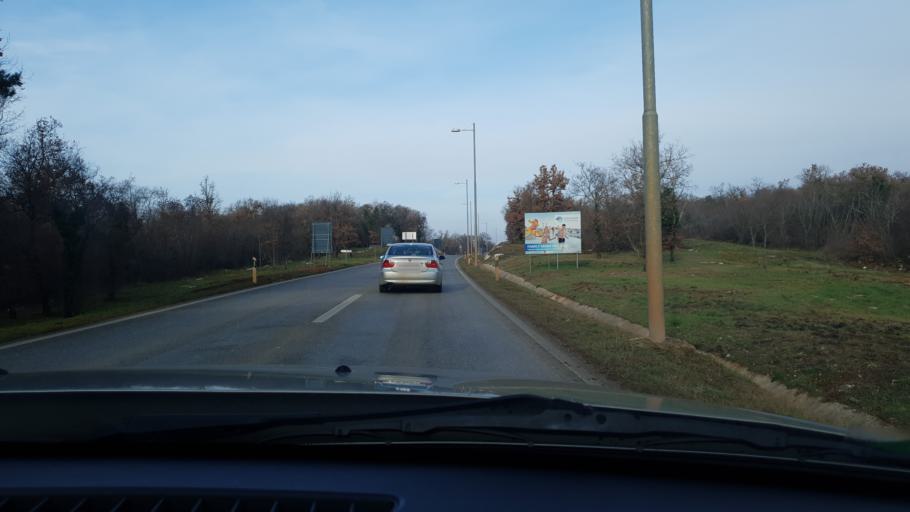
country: HR
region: Istarska
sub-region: Grad Porec
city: Porec
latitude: 45.2339
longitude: 13.6223
